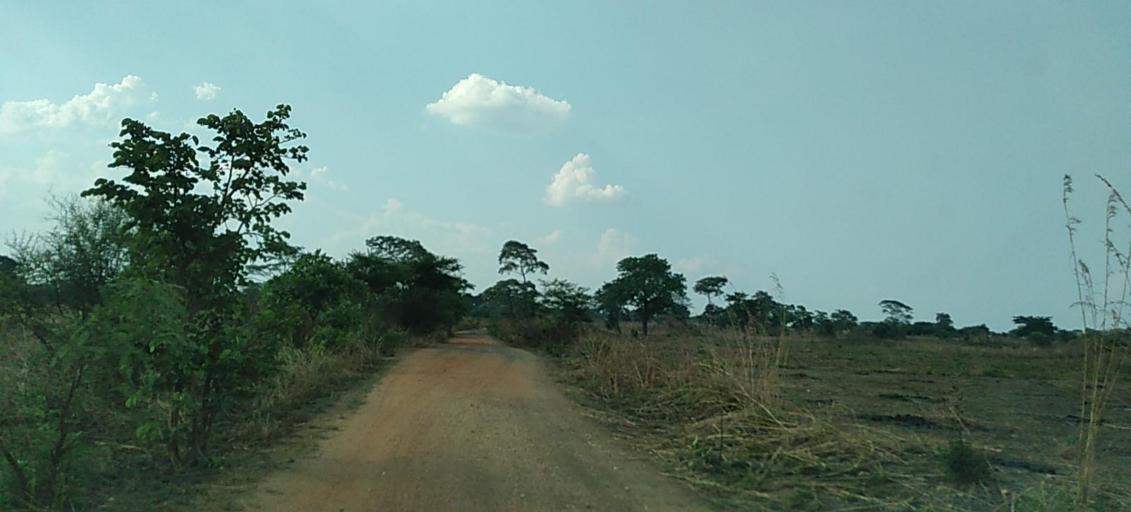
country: ZM
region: Copperbelt
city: Mpongwe
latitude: -13.4998
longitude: 28.0879
